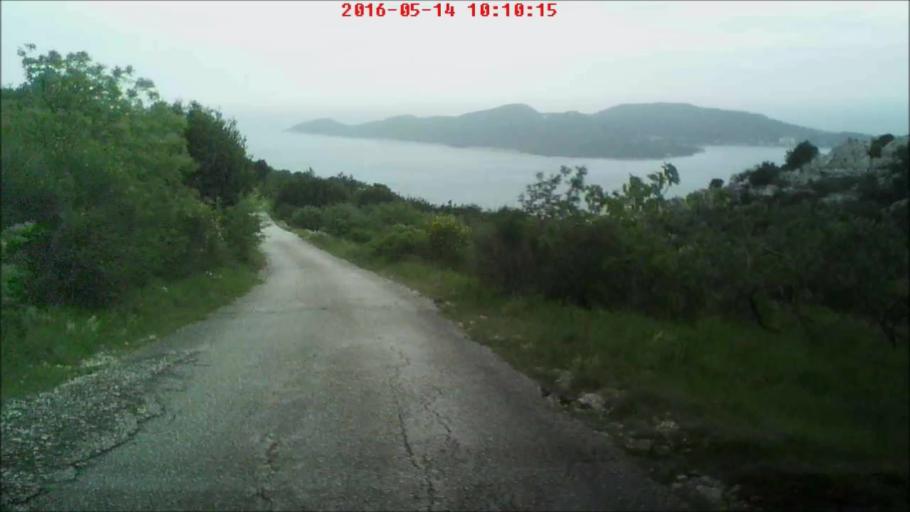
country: HR
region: Dubrovacko-Neretvanska
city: Podgora
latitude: 42.7408
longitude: 17.9396
